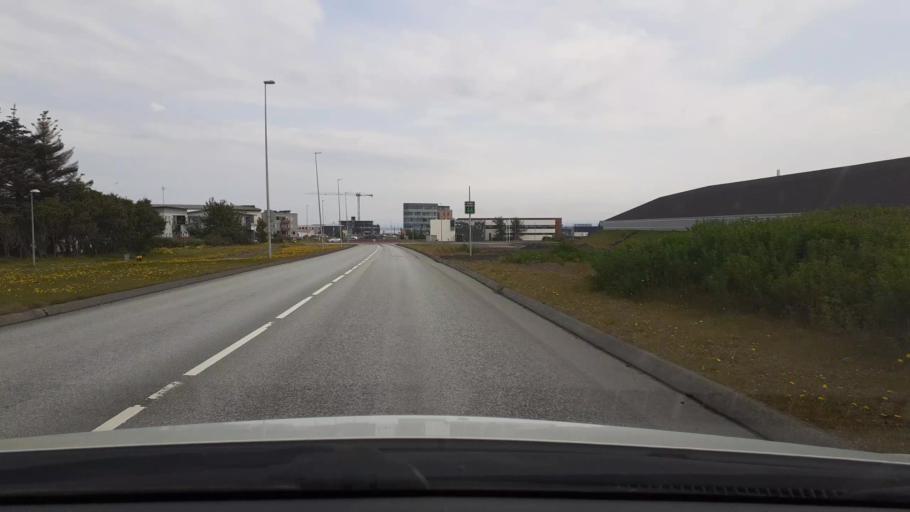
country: IS
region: Southern Peninsula
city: Reykjanesbaer
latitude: 63.9946
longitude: -22.5607
